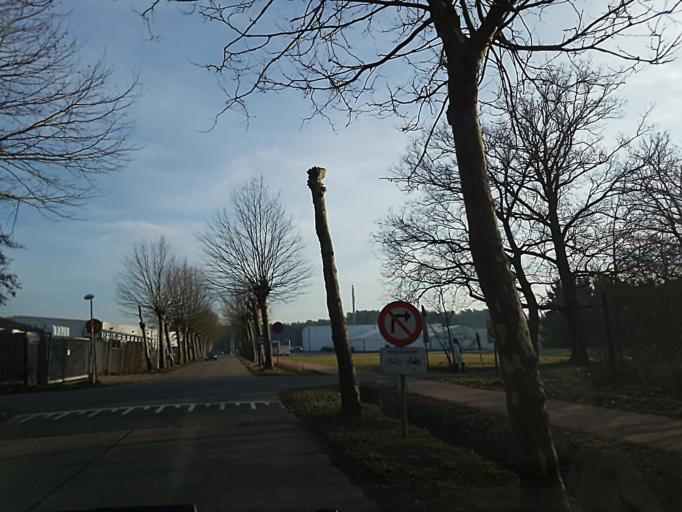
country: BE
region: Flanders
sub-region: Provincie Antwerpen
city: Schilde
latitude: 51.2513
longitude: 4.6037
